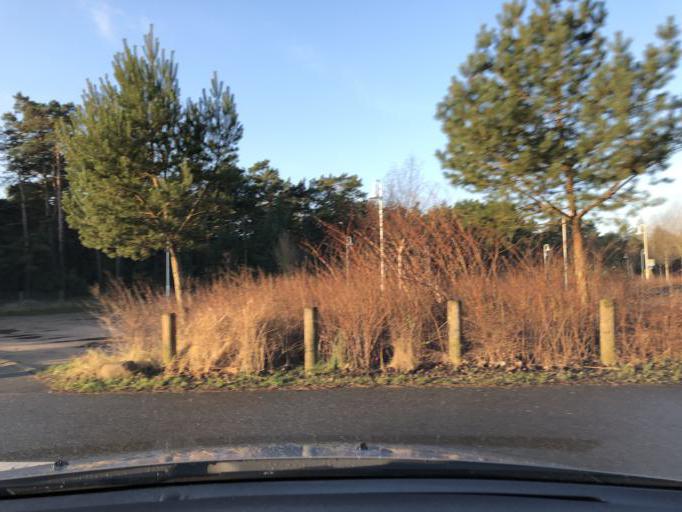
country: DE
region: Mecklenburg-Vorpommern
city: Ostseebad Prerow
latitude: 54.4517
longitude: 12.5548
